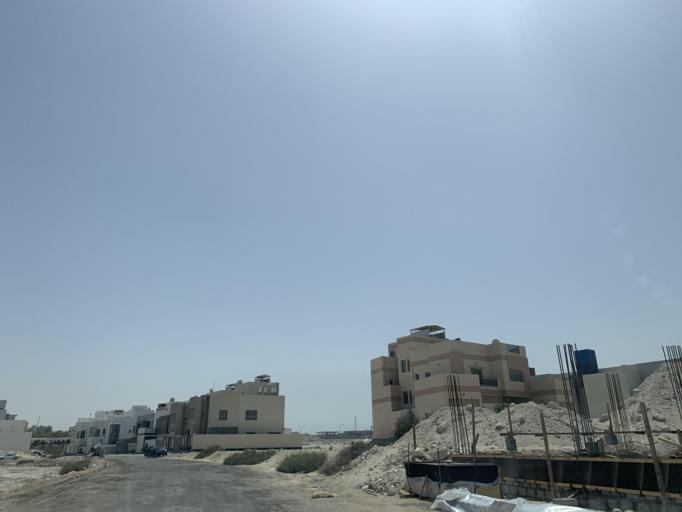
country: BH
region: Northern
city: Madinat `Isa
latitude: 26.1537
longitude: 50.5501
